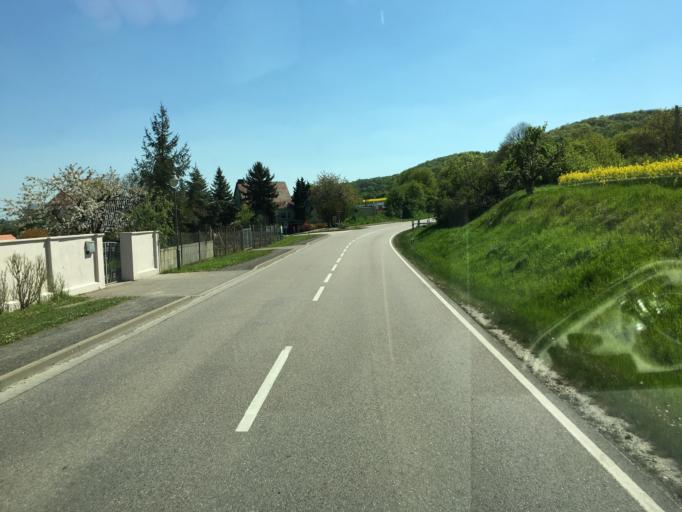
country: DE
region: Saxony-Anhalt
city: Freyburg
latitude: 51.2005
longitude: 11.7702
